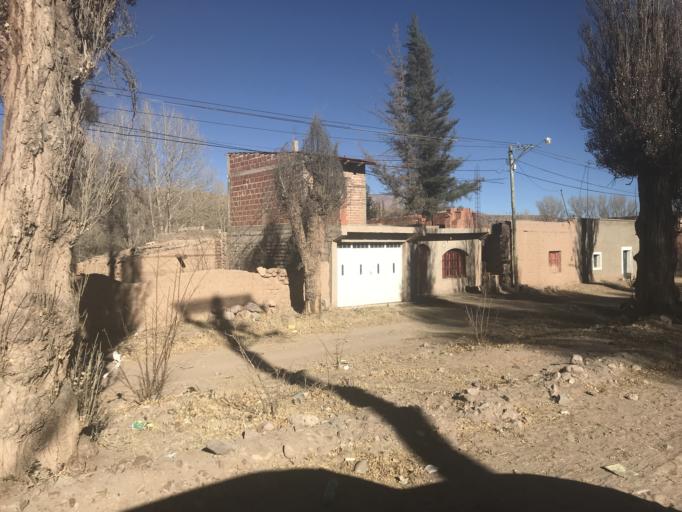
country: AR
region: Jujuy
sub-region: Departamento de Humahuaca
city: Humahuaca
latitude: -23.2120
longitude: -65.3467
